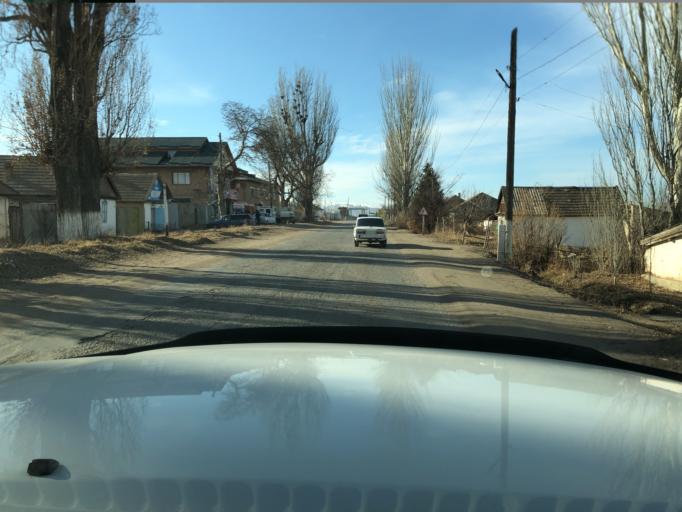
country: KG
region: Ysyk-Koel
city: Pokrovka
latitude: 42.3350
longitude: 77.9895
